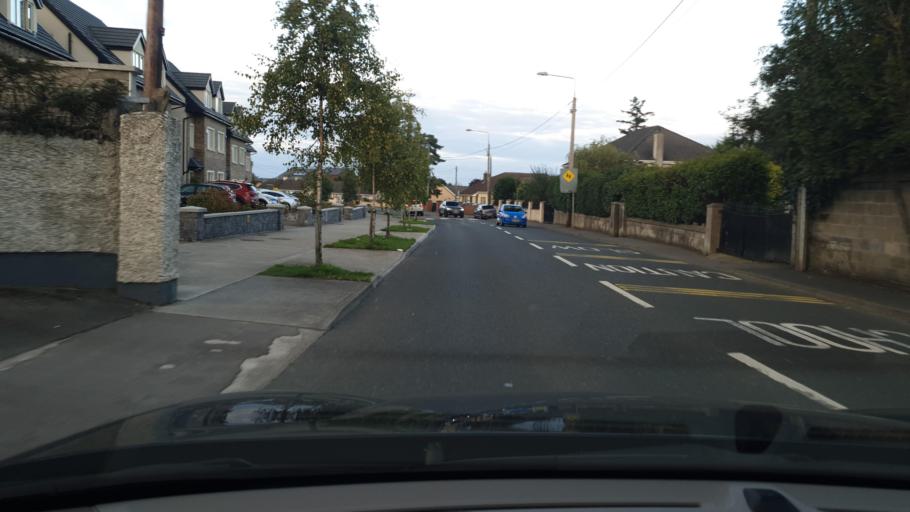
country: IE
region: Leinster
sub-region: South Dublin
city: Rathcoole
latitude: 53.2781
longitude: -6.4788
